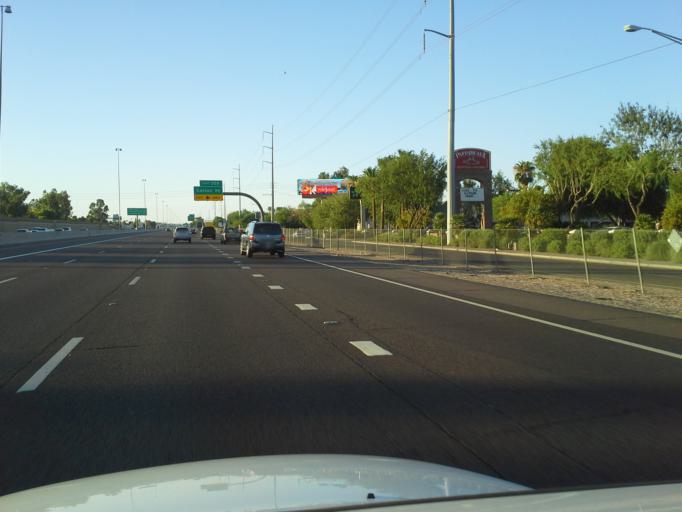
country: US
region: Arizona
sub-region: Maricopa County
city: Glendale
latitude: 33.5872
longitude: -112.1168
